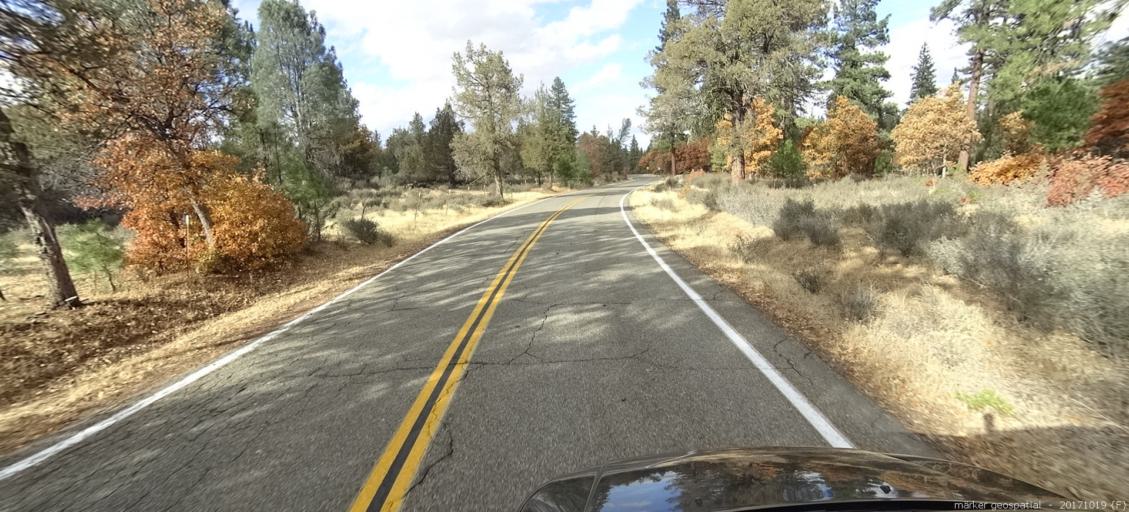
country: US
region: California
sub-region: Shasta County
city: Burney
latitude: 40.9550
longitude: -121.4405
